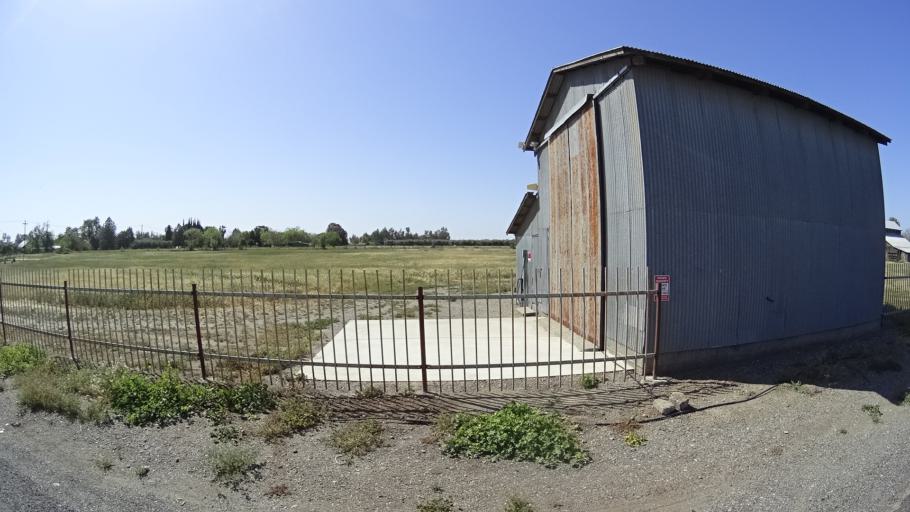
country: US
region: California
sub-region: Glenn County
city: Orland
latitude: 39.7256
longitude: -122.1893
